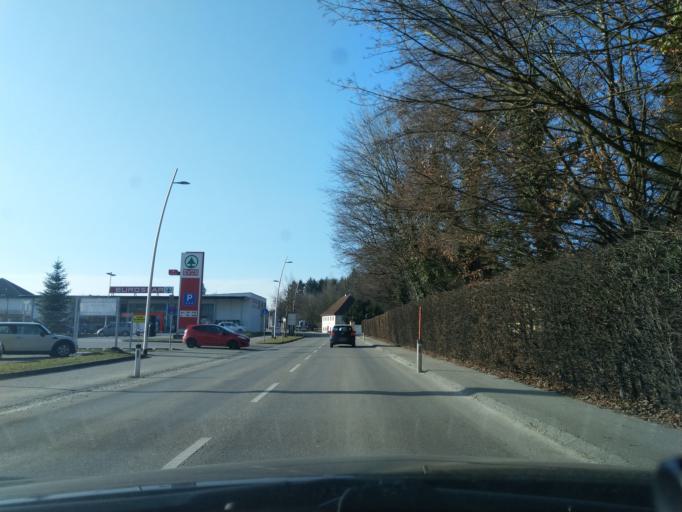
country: AT
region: Upper Austria
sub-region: Politischer Bezirk Scharding
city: Sankt Marienkirchen bei Schaerding
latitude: 48.2945
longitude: 13.4373
